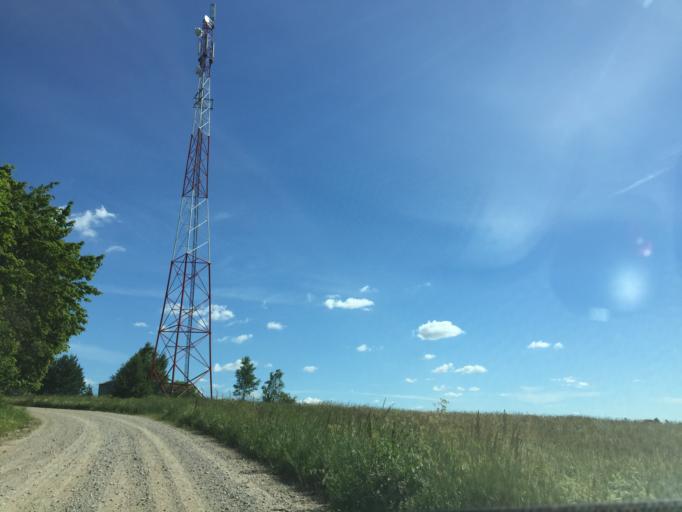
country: LV
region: Dundaga
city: Dundaga
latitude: 57.3556
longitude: 22.0311
